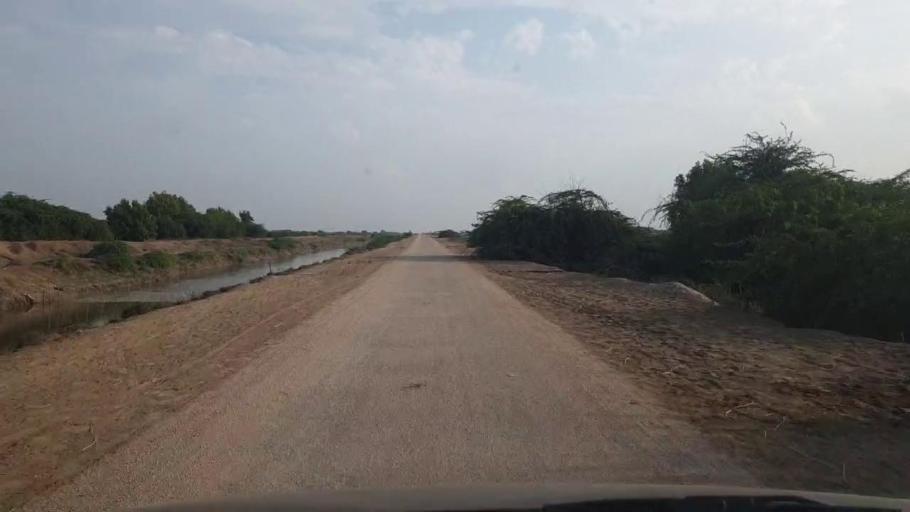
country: PK
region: Sindh
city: Badin
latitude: 24.5468
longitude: 68.6717
